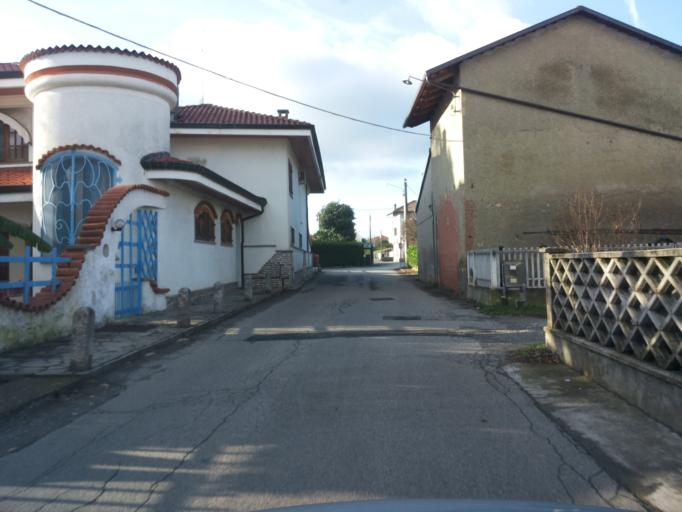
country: IT
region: Piedmont
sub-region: Provincia di Vercelli
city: Alice Castello
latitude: 45.3709
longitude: 8.0755
